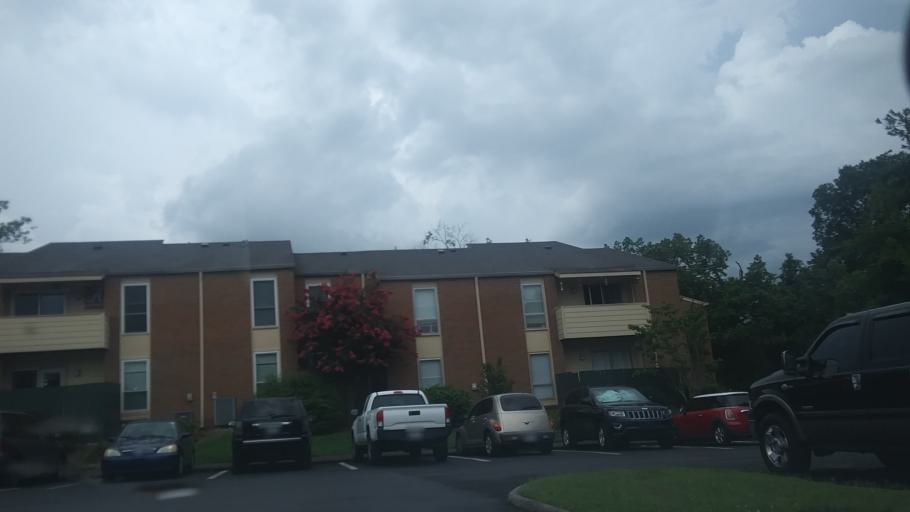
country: US
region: Tennessee
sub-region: Davidson County
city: Belle Meade
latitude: 36.1571
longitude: -86.8865
